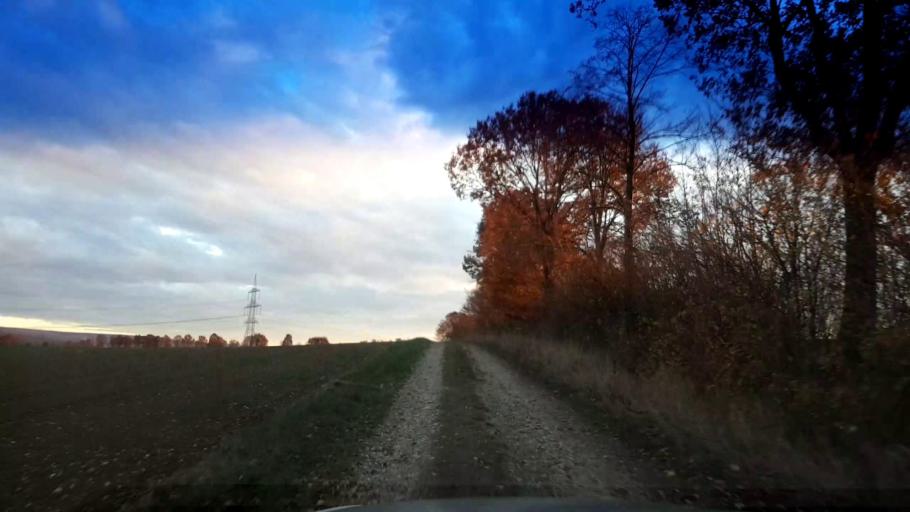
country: DE
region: Bavaria
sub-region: Upper Franconia
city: Memmelsdorf
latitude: 49.9633
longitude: 10.9765
